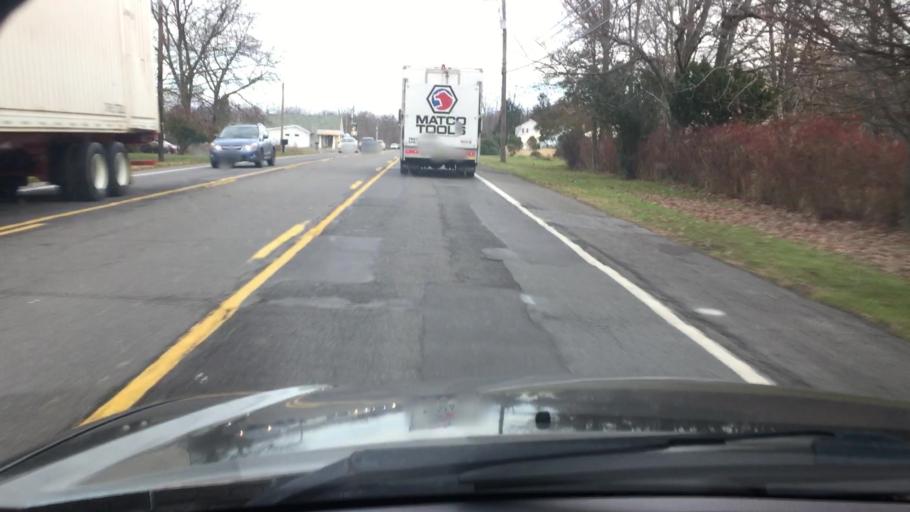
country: US
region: Pennsylvania
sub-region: Luzerne County
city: Mountain Top
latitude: 41.1264
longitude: -75.9073
